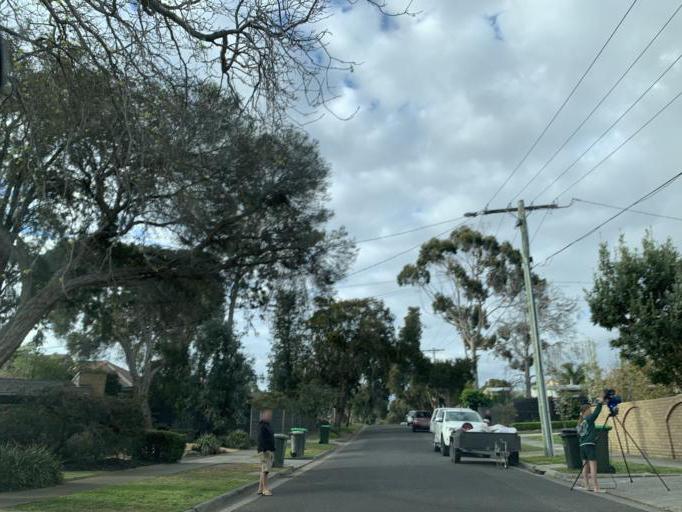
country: AU
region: Victoria
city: Beaumaris
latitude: -37.9811
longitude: 145.0409
